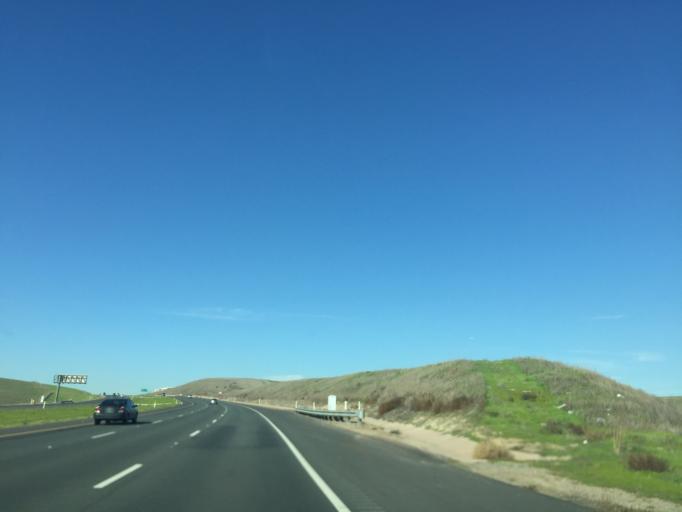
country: US
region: California
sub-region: San Diego County
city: Bonita
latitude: 32.6030
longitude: -116.9645
